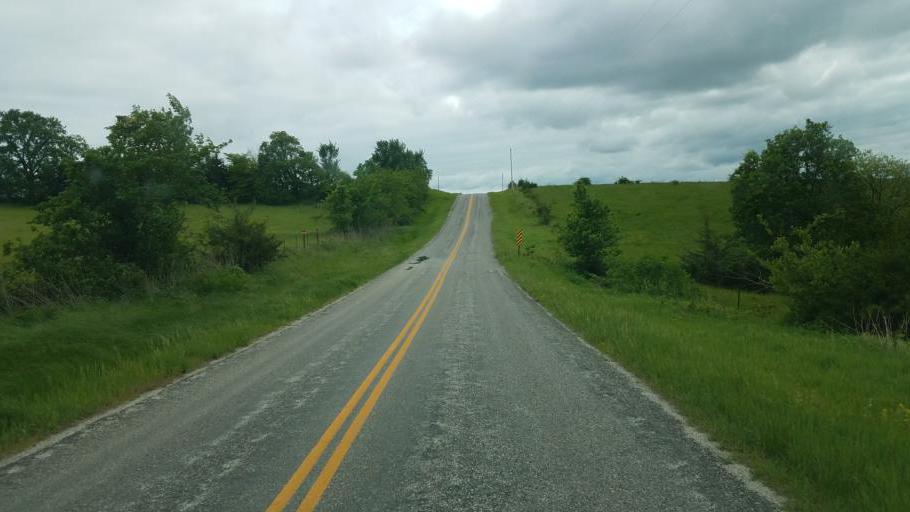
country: US
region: Iowa
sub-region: Decatur County
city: Lamoni
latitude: 40.5605
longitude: -93.8409
